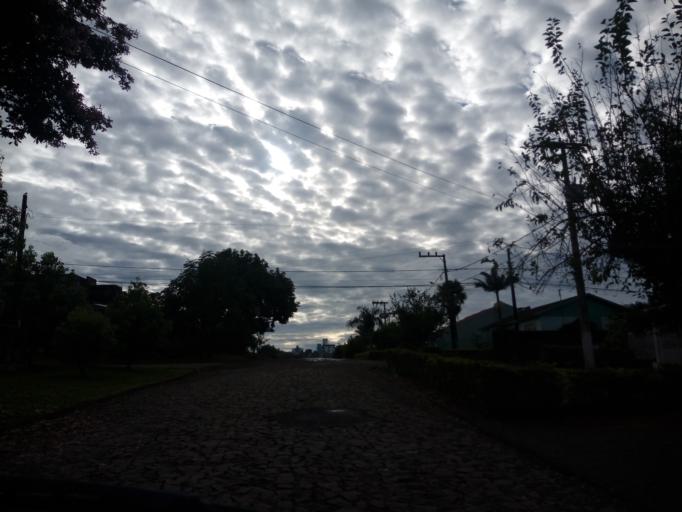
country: BR
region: Santa Catarina
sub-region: Chapeco
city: Chapeco
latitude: -27.1090
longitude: -52.6336
